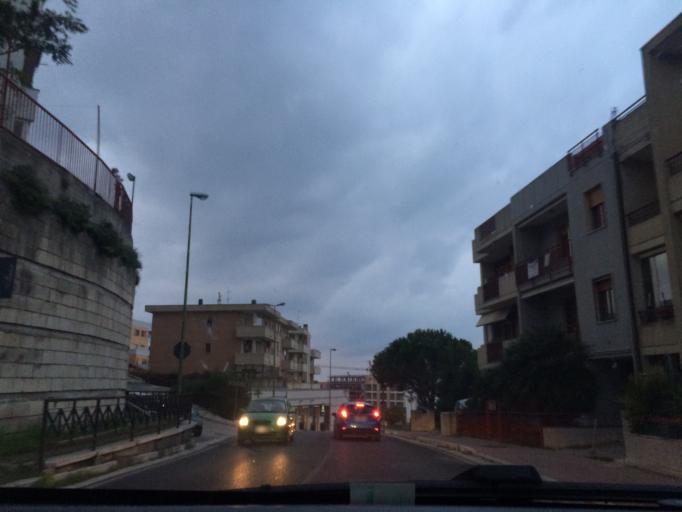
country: IT
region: Basilicate
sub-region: Provincia di Matera
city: Matera
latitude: 40.6716
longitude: 16.5923
